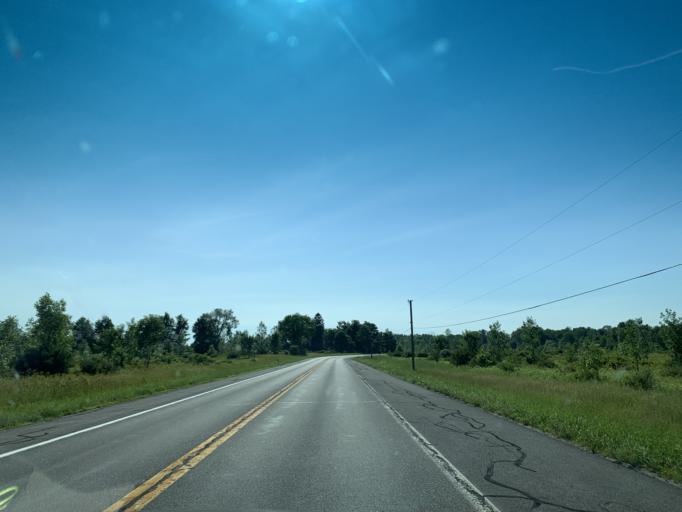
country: US
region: New York
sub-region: Oneida County
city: Sherrill
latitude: 43.1345
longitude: -75.6027
